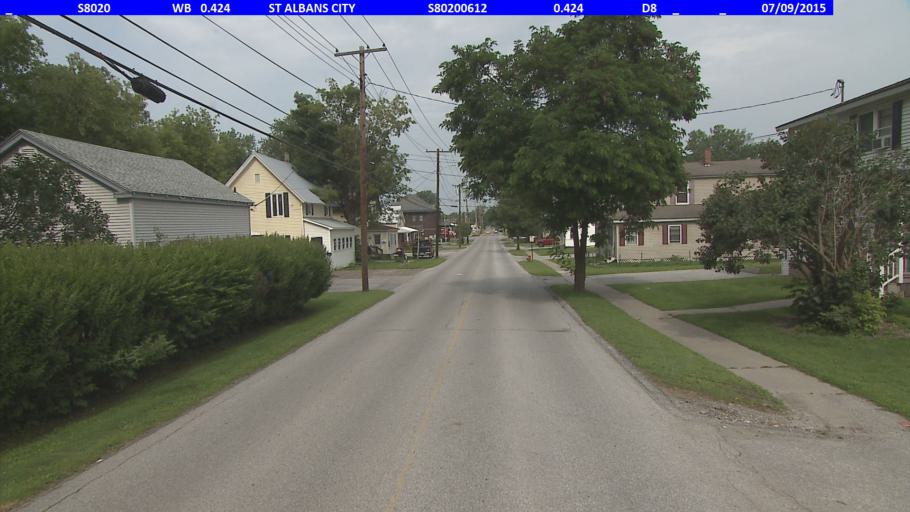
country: US
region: Vermont
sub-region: Franklin County
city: Saint Albans
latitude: 44.8069
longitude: -73.0856
